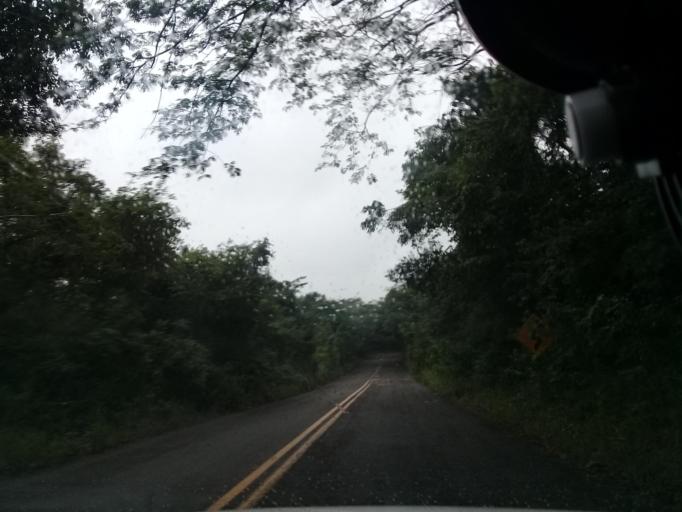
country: MX
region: Veracruz
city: Platon Sanchez
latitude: 21.2364
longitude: -98.3691
